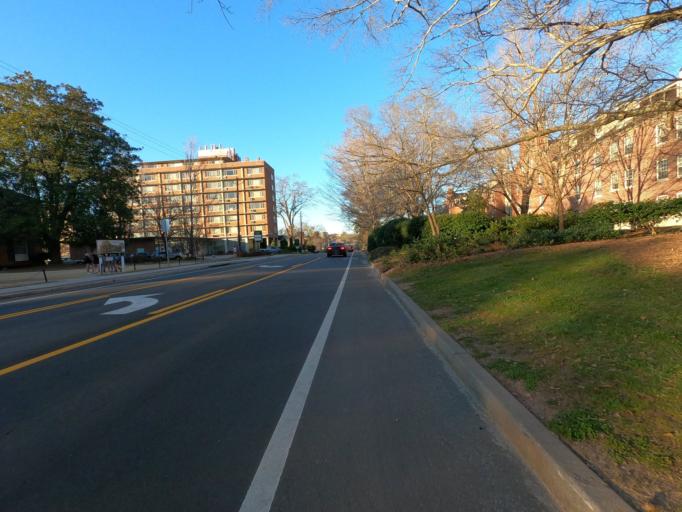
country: US
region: Georgia
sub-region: Clarke County
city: Athens
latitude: 33.9461
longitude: -83.3785
